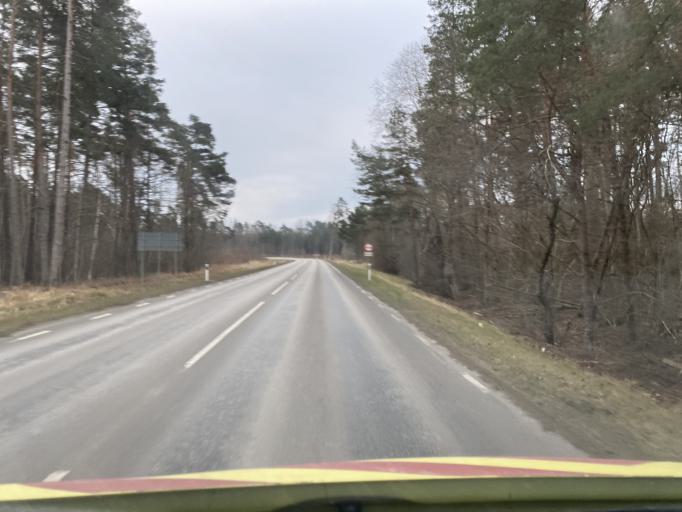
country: EE
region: Laeaene
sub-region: Ridala Parish
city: Uuemoisa
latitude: 58.9069
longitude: 23.5634
